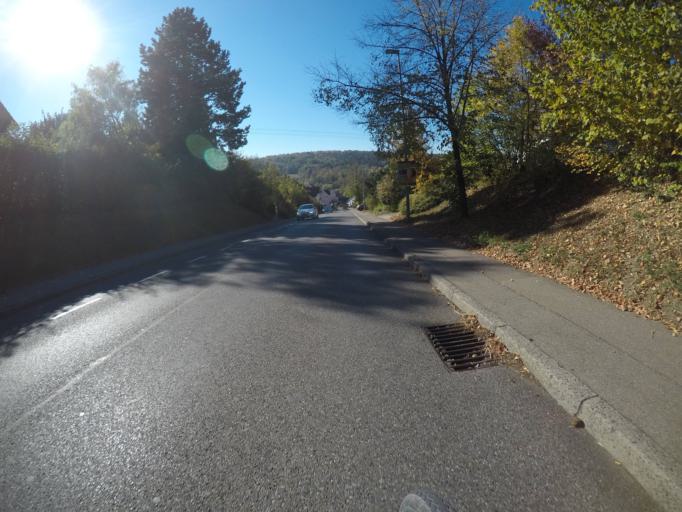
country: DE
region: Baden-Wuerttemberg
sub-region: Regierungsbezirk Stuttgart
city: Schlaitdorf
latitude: 48.6226
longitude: 9.2357
